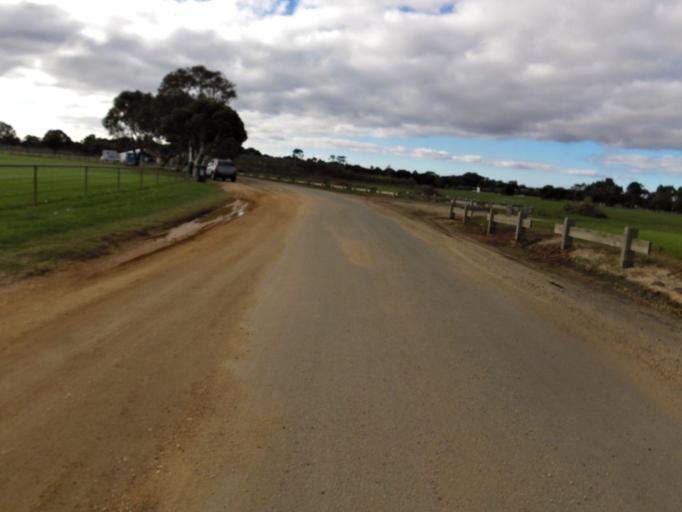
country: AU
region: Victoria
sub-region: Greater Geelong
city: Breakwater
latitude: -38.1840
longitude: 144.3575
